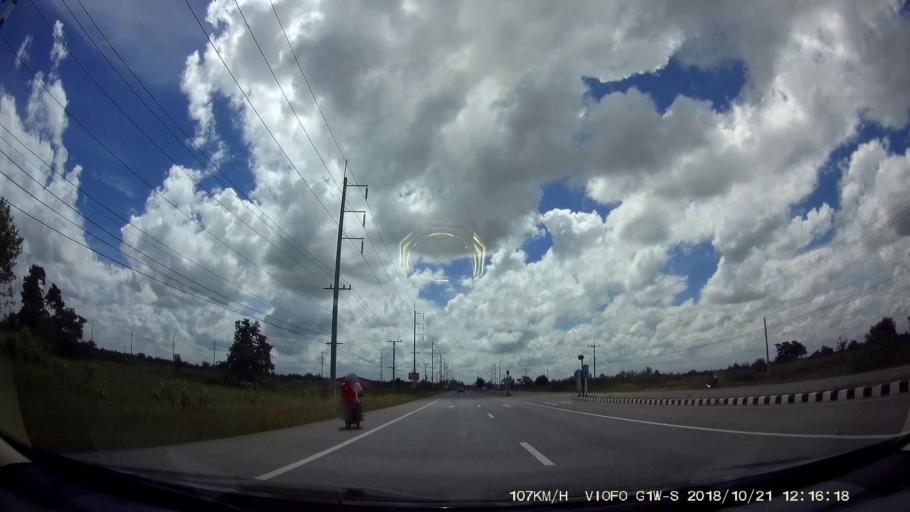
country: TH
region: Nakhon Ratchasima
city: Dan Khun Thot
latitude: 15.3496
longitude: 101.8265
